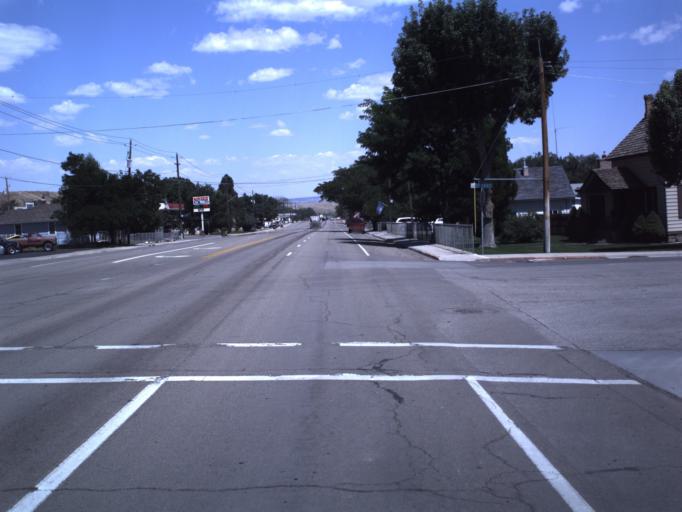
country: US
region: Utah
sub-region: Emery County
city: Castle Dale
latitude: 39.2117
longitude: -111.0162
